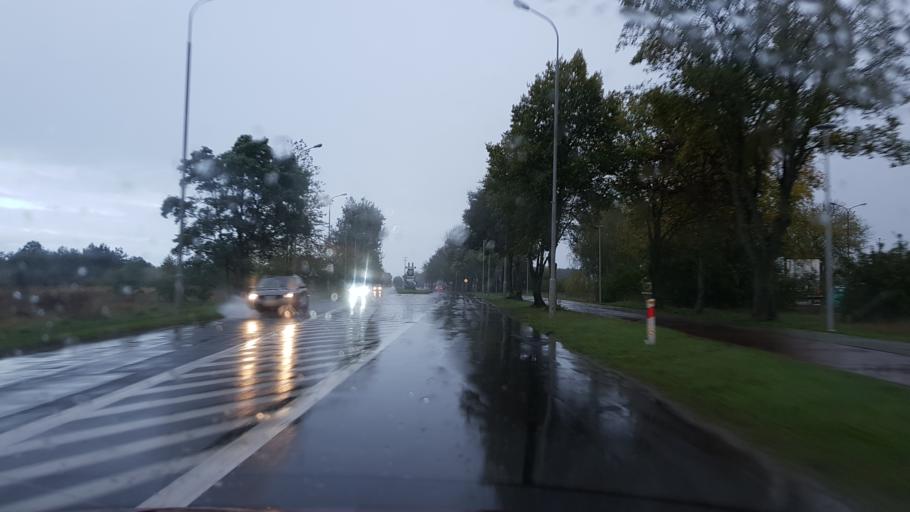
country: PL
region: Greater Poland Voivodeship
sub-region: Powiat pilski
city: Pila
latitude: 53.1545
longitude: 16.6916
